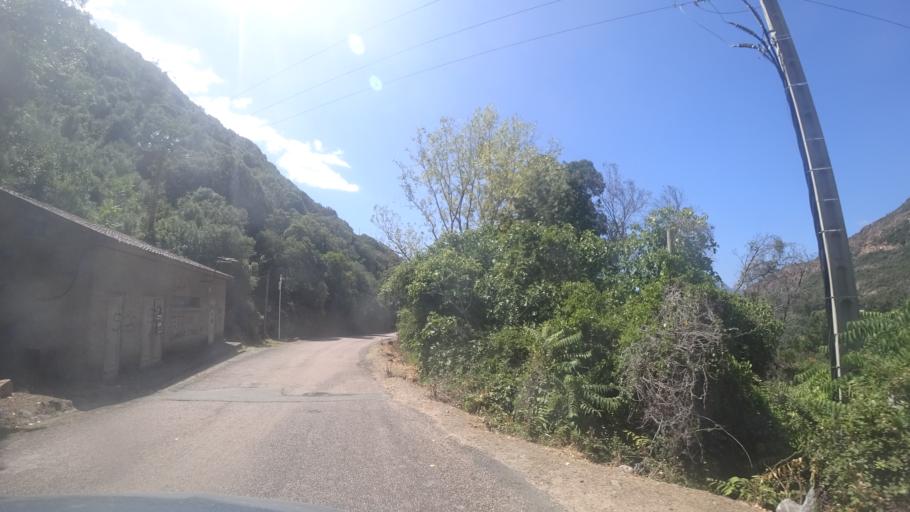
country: FR
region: Corsica
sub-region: Departement de la Corse-du-Sud
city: Cargese
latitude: 42.2630
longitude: 8.7014
